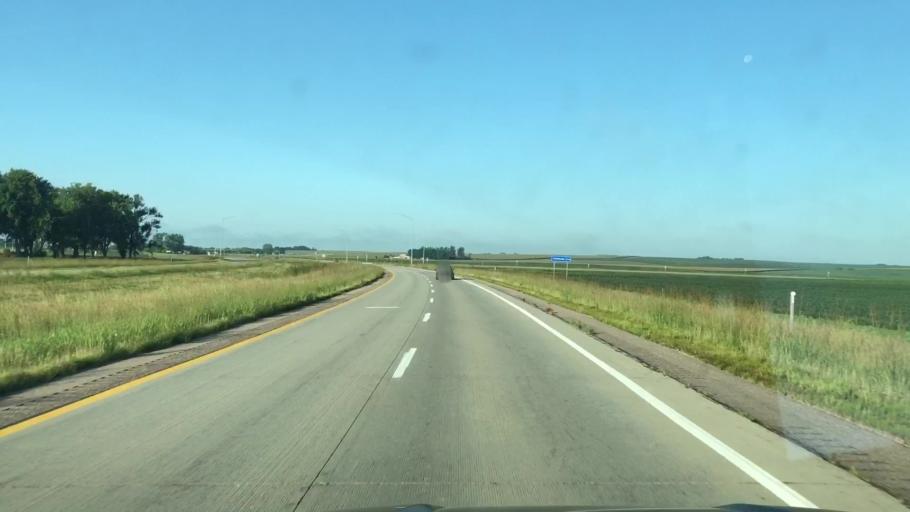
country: US
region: Iowa
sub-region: Sioux County
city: Alton
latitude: 42.9311
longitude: -96.0544
